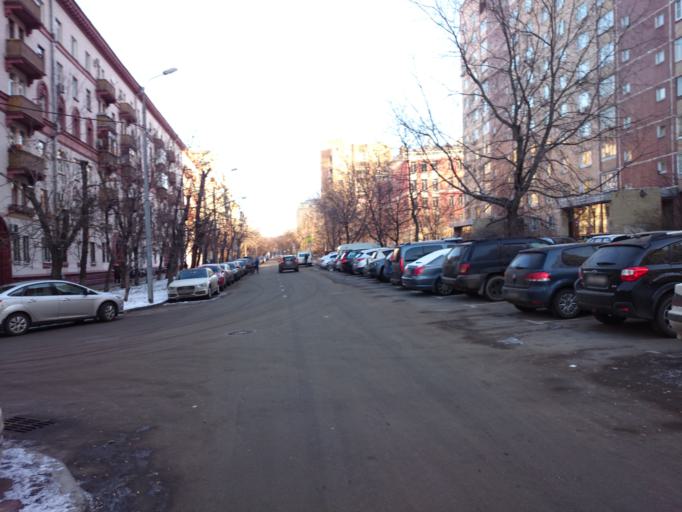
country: RU
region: Moscow
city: Sokol
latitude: 55.7997
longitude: 37.5234
